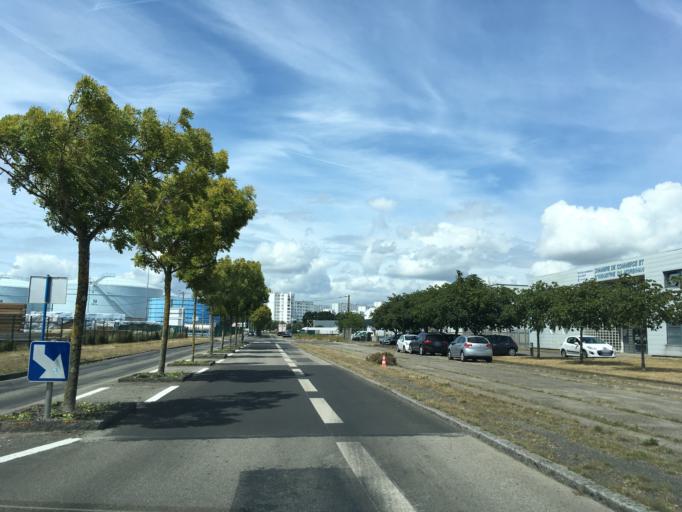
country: FR
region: Brittany
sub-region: Departement du Morbihan
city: Lorient
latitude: 47.7383
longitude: -3.3558
